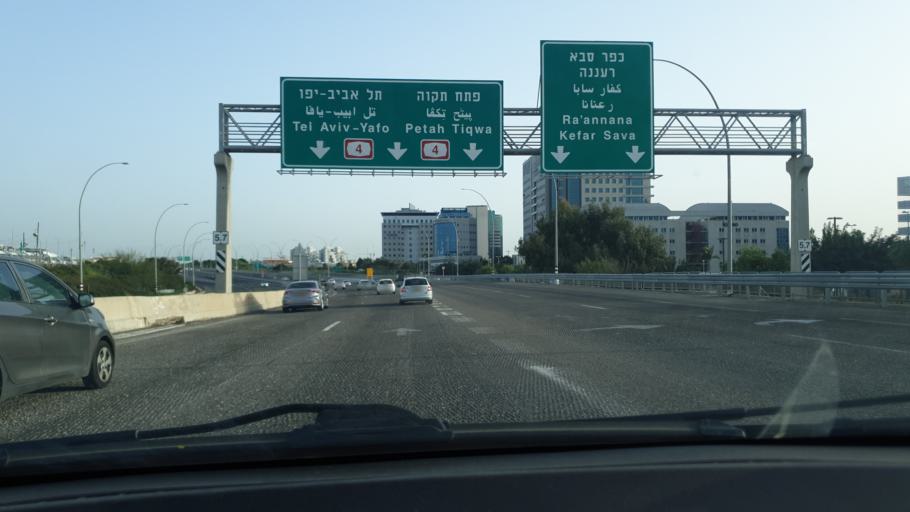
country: IL
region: Central District
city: Ra'anana
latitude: 32.1993
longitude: 34.8847
